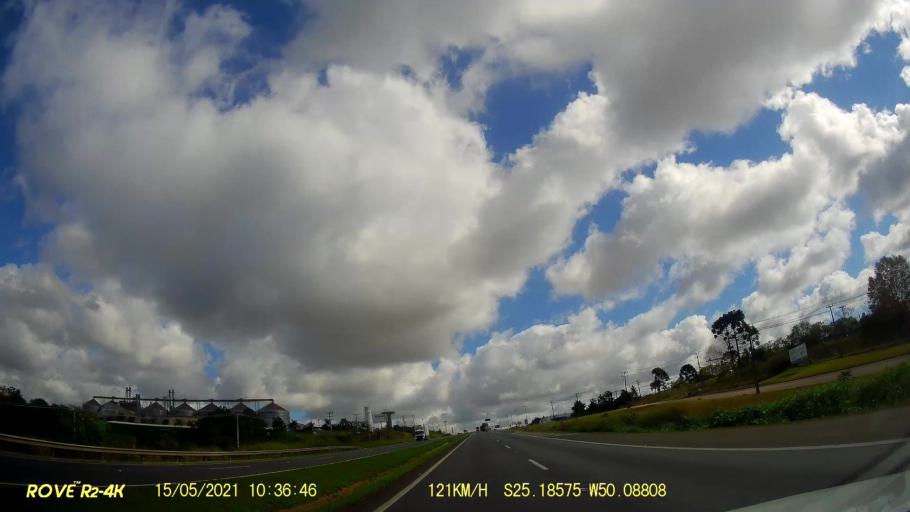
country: BR
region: Parana
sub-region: Ponta Grossa
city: Ponta Grossa
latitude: -25.1858
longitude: -50.0877
